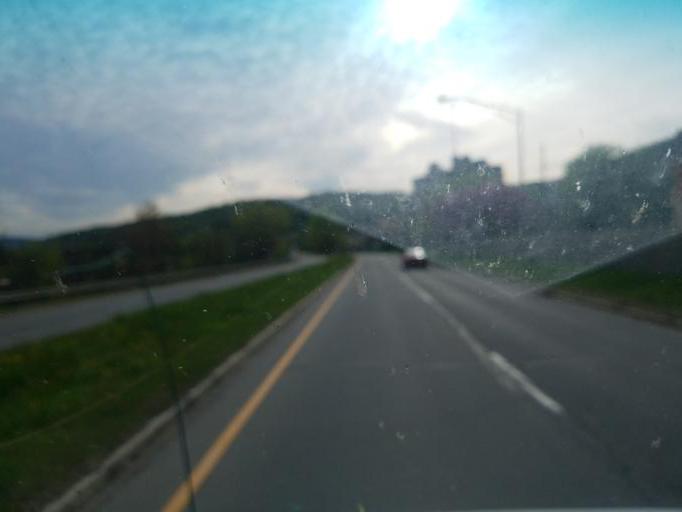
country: US
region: New York
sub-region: Herkimer County
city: Little Falls
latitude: 43.0425
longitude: -74.8545
